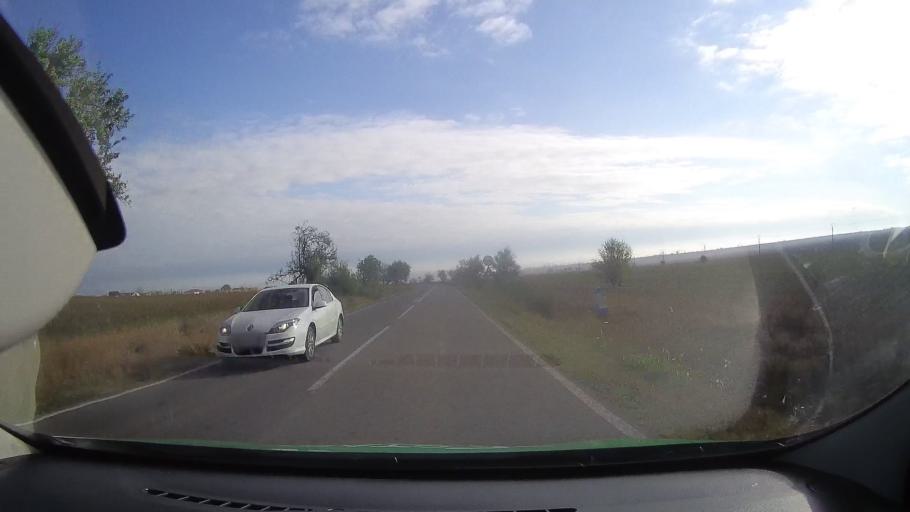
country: RO
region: Tulcea
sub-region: Comuna Mahmudia
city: Mahmudia
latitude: 45.0774
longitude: 29.0719
